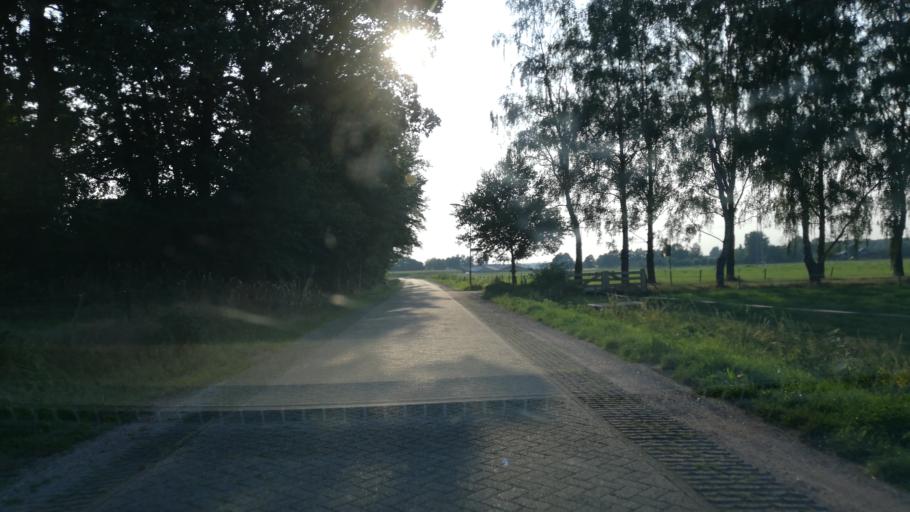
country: NL
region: Gelderland
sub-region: Gemeente Ermelo
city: Horst
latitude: 52.2806
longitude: 5.5694
